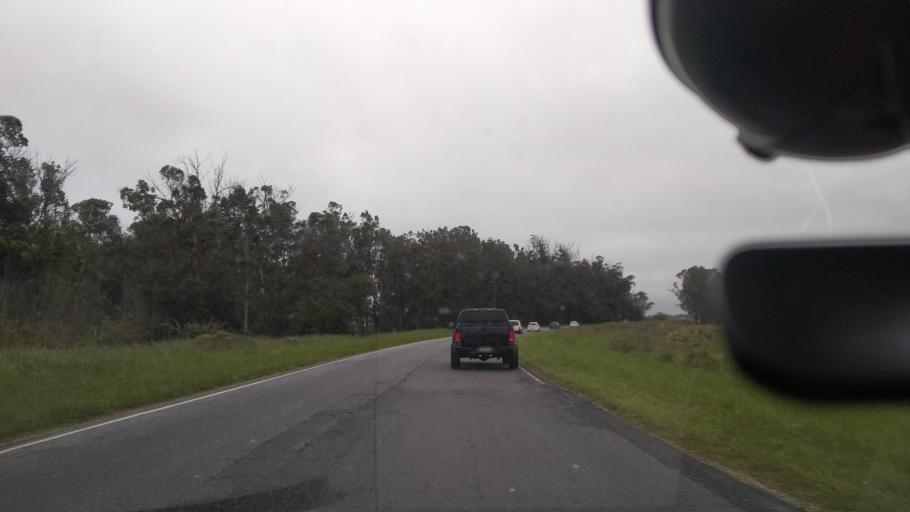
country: AR
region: Buenos Aires
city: Veronica
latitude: -35.5116
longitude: -57.3361
